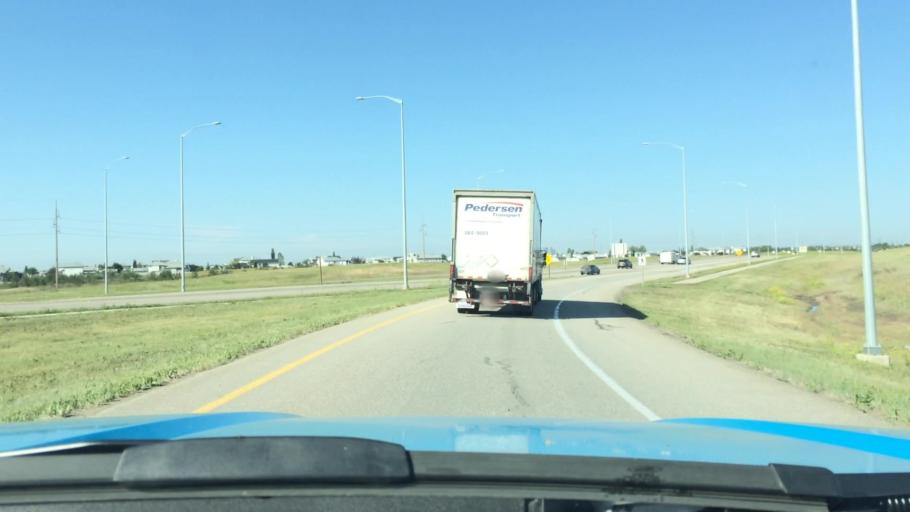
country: CA
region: Alberta
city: Chestermere
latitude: 51.0974
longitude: -113.9239
